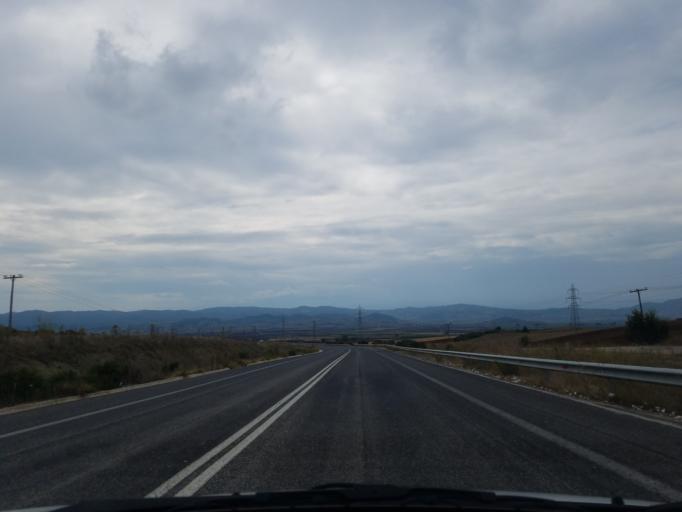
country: GR
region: Central Greece
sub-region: Nomos Fthiotidos
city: Domokos
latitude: 39.0971
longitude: 22.3049
